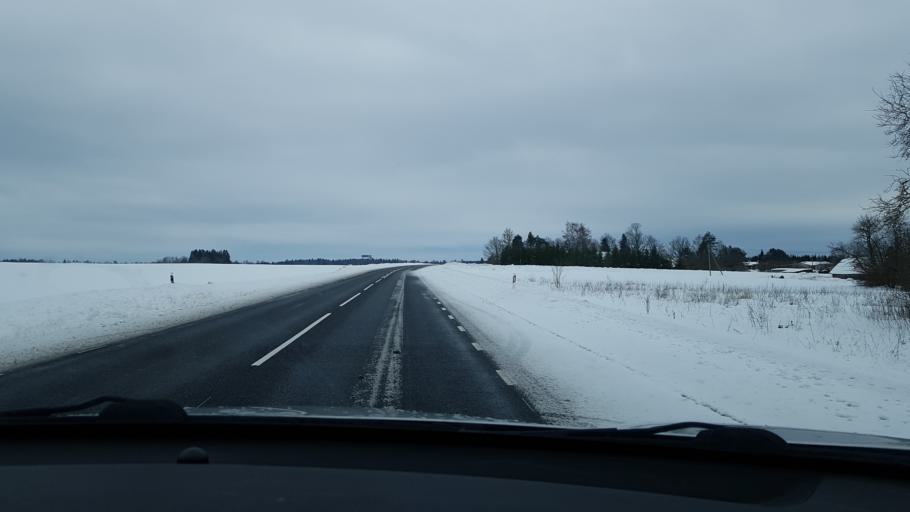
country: EE
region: Jaervamaa
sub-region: Jaerva-Jaani vald
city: Jarva-Jaani
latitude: 59.1180
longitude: 25.7914
